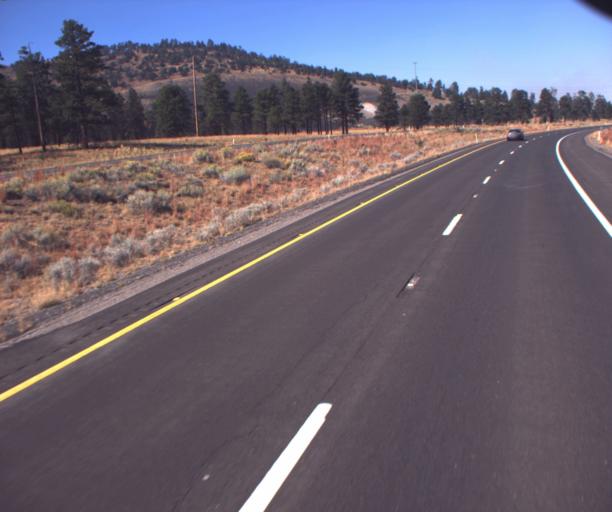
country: US
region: Arizona
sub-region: Coconino County
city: Flagstaff
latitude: 35.3797
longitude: -111.5798
